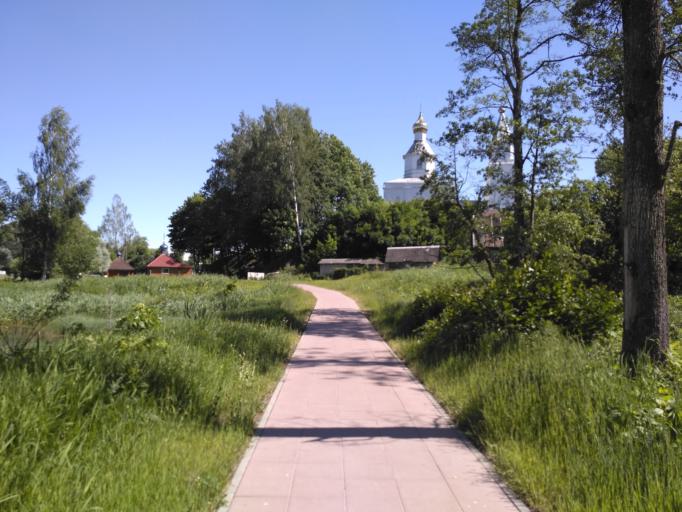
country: BY
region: Minsk
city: Lahoysk
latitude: 54.2028
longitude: 27.8489
